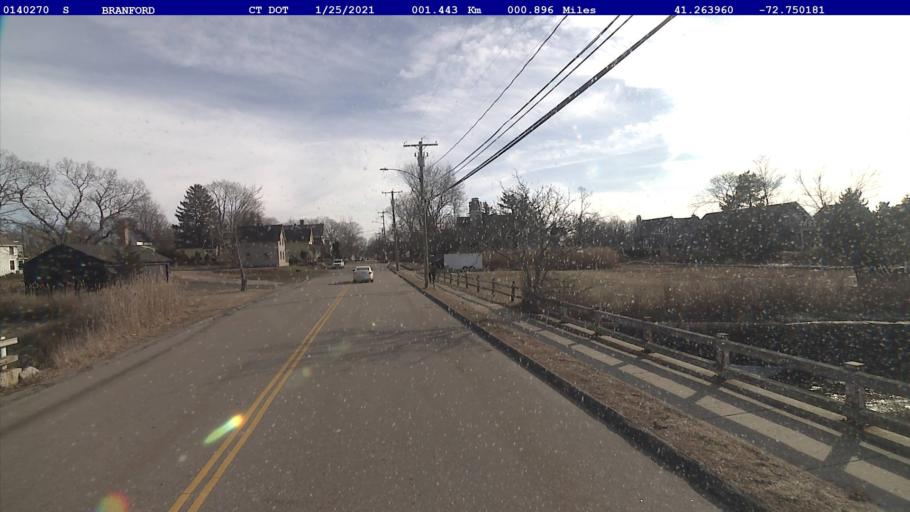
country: US
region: Connecticut
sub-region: New Haven County
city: North Branford
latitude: 41.2640
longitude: -72.7502
